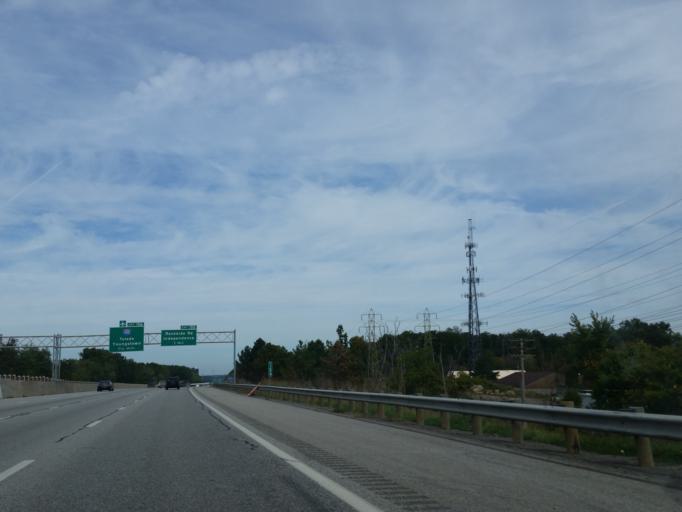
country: US
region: Ohio
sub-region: Cuyahoga County
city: Independence
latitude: 41.3751
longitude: -81.6523
